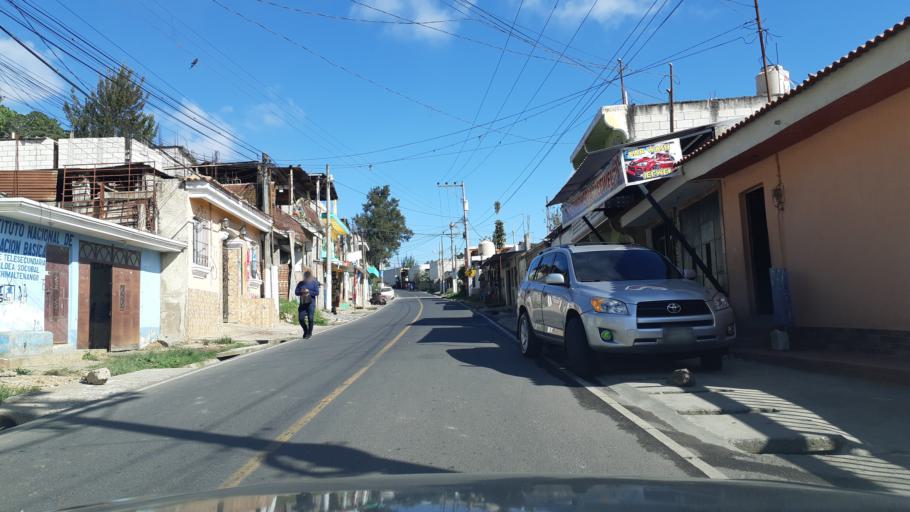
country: GT
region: Chimaltenango
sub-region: Municipio de Chimaltenango
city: Chimaltenango
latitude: 14.6515
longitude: -90.8203
